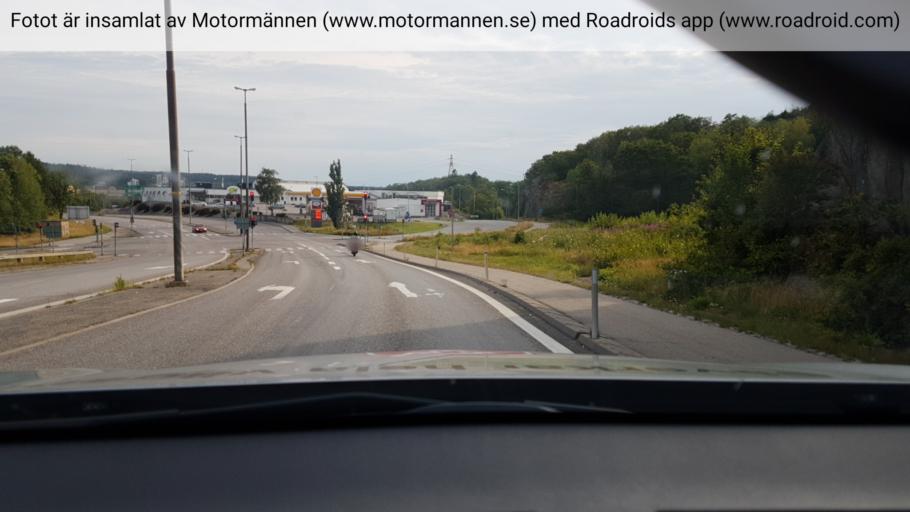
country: SE
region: Vaestra Goetaland
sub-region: Uddevalla Kommun
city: Uddevalla
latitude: 58.3574
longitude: 11.9662
